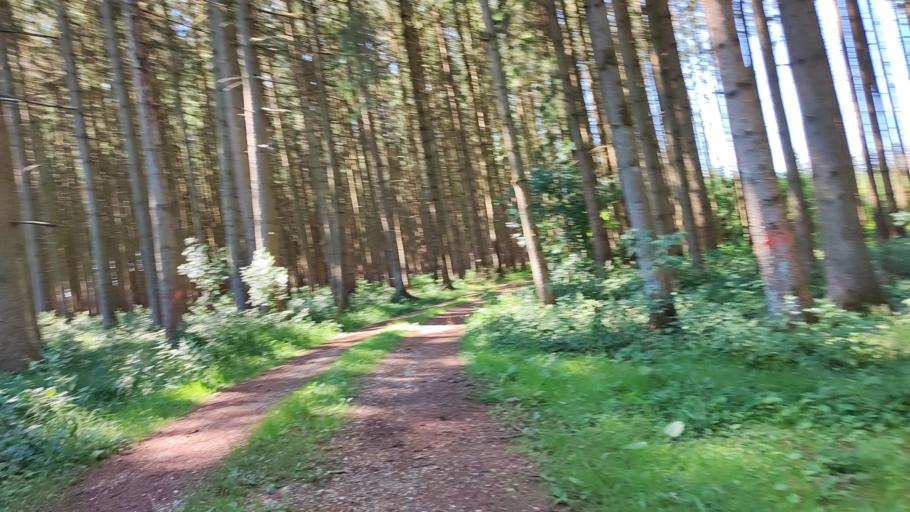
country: DE
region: Bavaria
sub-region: Swabia
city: Landensberg
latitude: 48.4605
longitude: 10.5296
